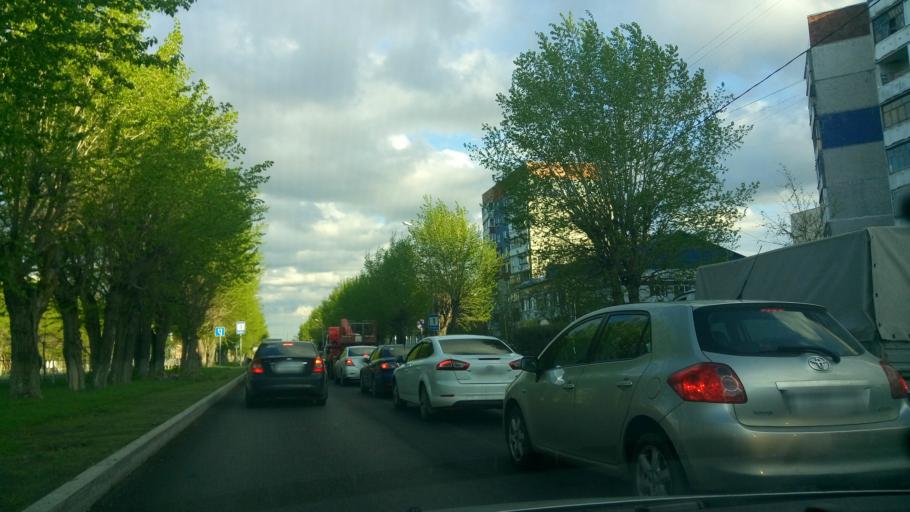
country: RU
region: Tjumen
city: Tyumen
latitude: 57.1362
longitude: 65.5994
